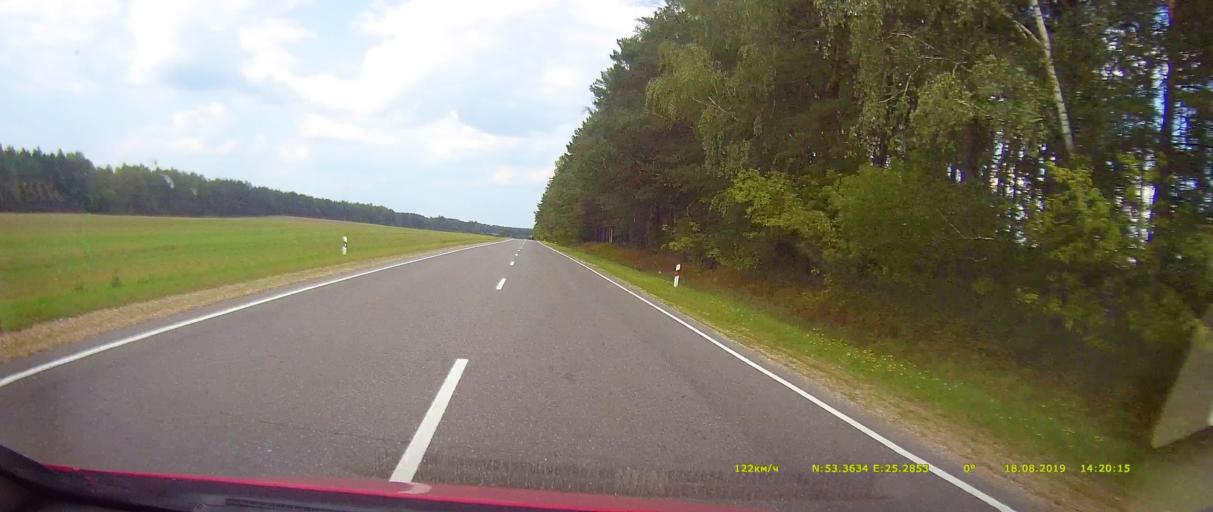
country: BY
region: Grodnenskaya
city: Dzyatlava
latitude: 53.3815
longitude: 25.2903
